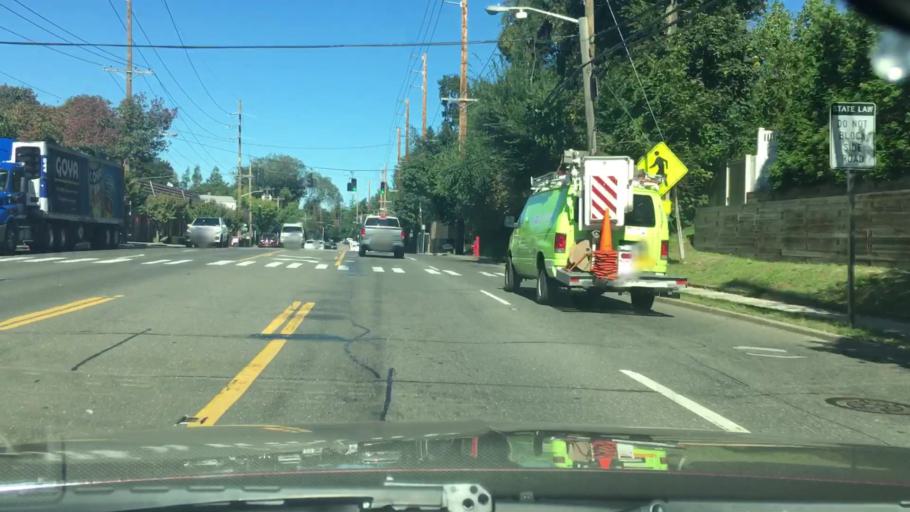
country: US
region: New York
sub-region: Nassau County
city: Flower Hill
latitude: 40.8177
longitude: -73.6798
